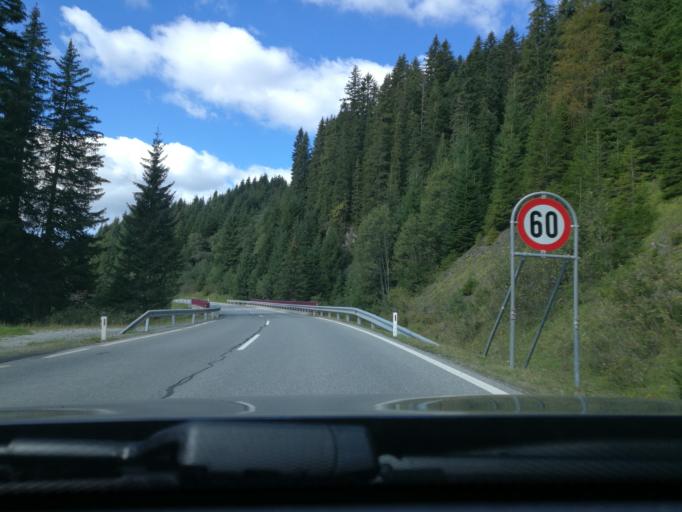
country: AT
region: Salzburg
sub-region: Politischer Bezirk Zell am See
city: Krimml
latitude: 47.2440
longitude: 12.0998
